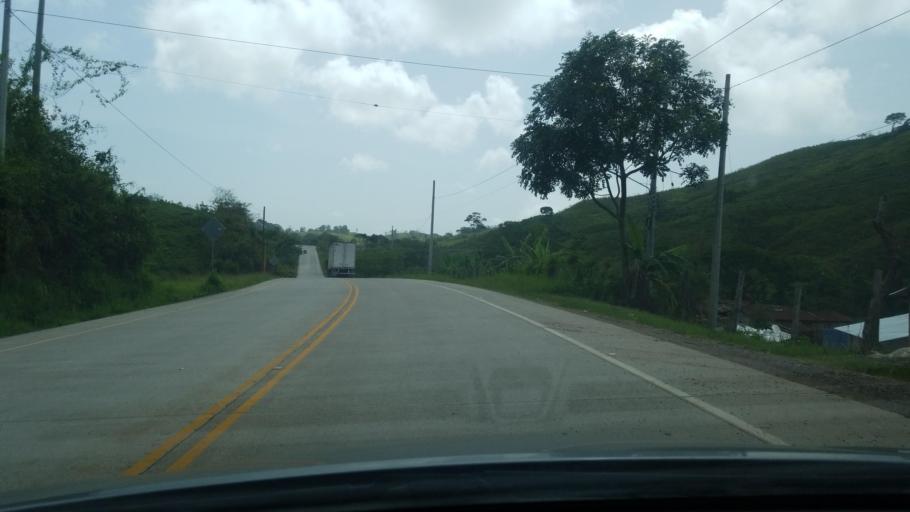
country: HN
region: Copan
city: San Jeronimo
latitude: 14.9354
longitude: -88.9216
